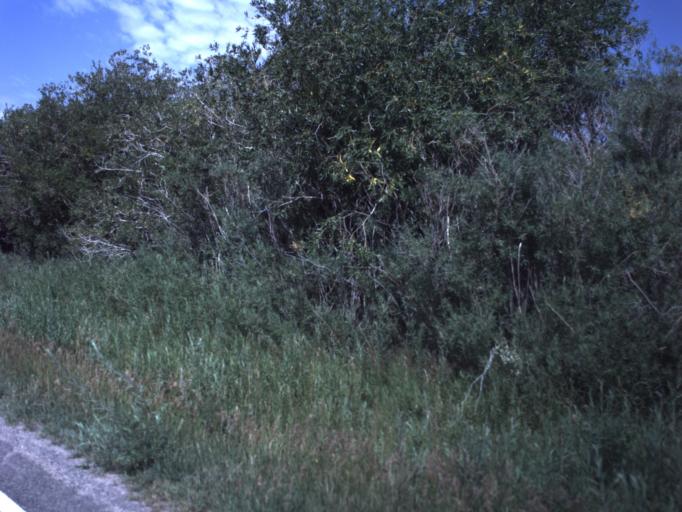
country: US
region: Utah
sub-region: Daggett County
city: Manila
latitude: 40.9781
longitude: -109.8157
